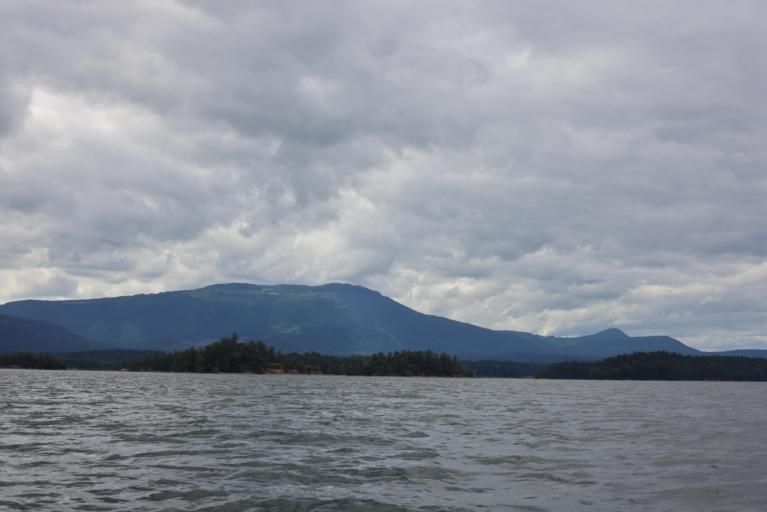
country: CA
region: British Columbia
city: North Cowichan
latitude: 48.8877
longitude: -123.6341
